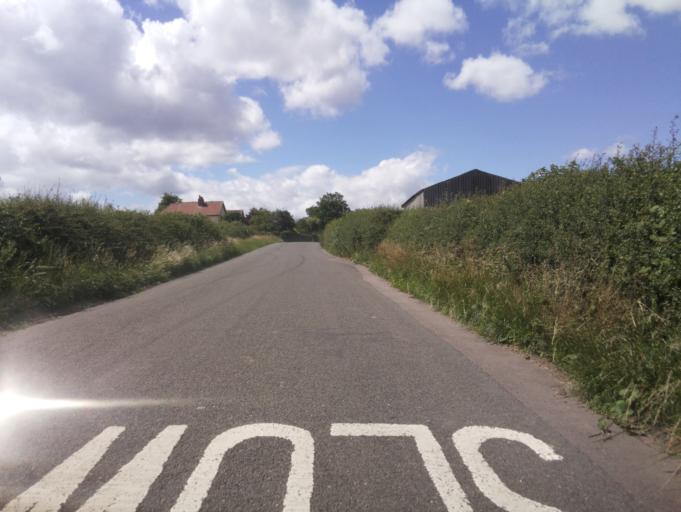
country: GB
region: England
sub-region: Nottinghamshire
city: Burton Joyce
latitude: 53.0038
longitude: -1.0735
